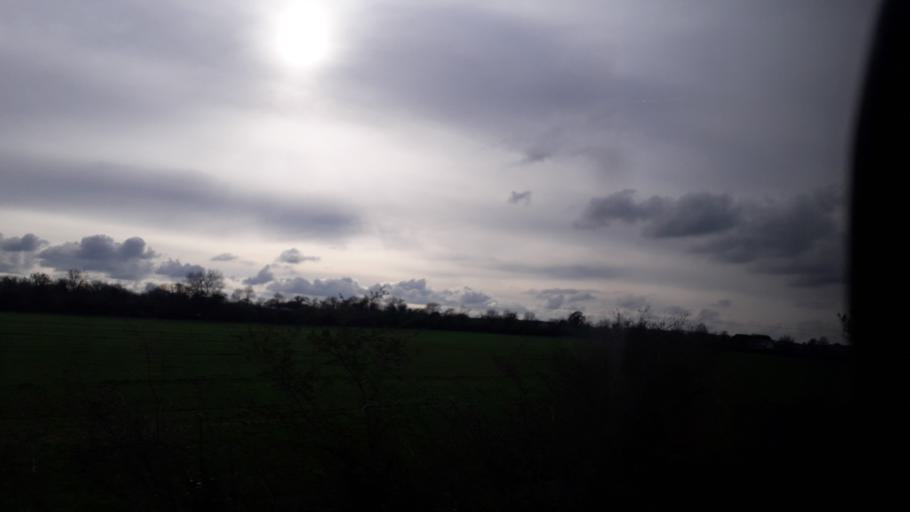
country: IE
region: Leinster
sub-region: Kildare
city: Kilcock
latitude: 53.3928
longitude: -6.6511
